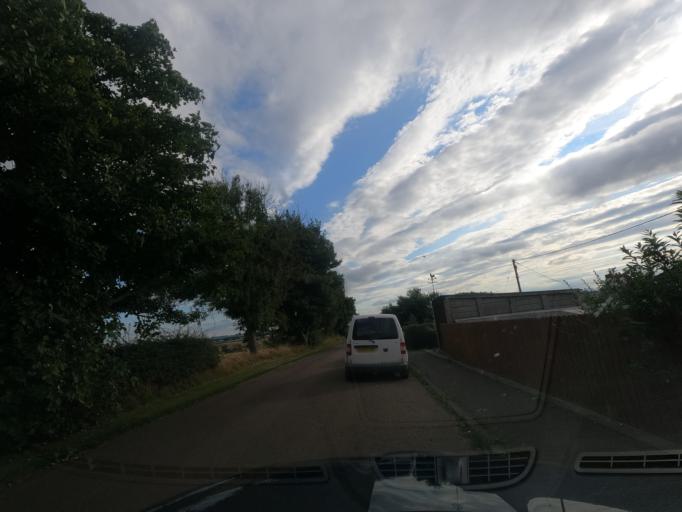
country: GB
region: England
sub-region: Northumberland
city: Ancroft
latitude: 55.7118
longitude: -2.0718
